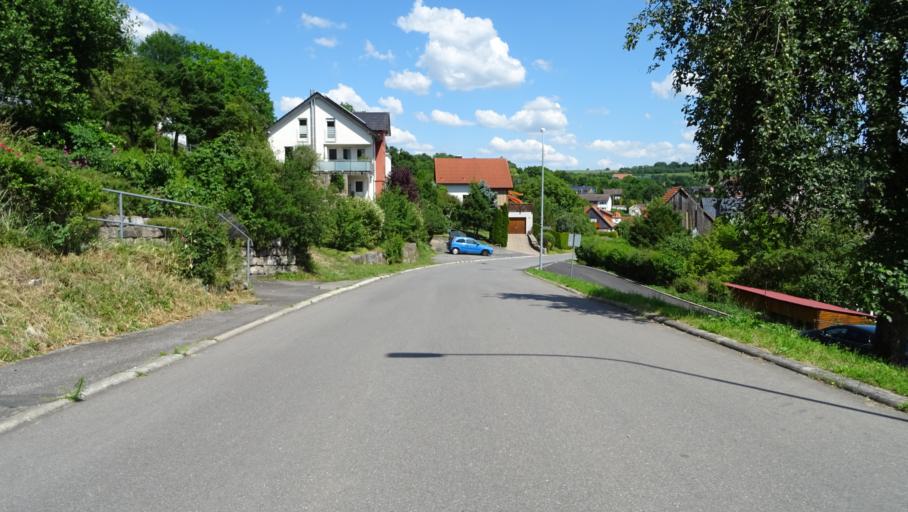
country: DE
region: Baden-Wuerttemberg
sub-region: Karlsruhe Region
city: Adelsheim
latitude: 49.3825
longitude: 9.3764
